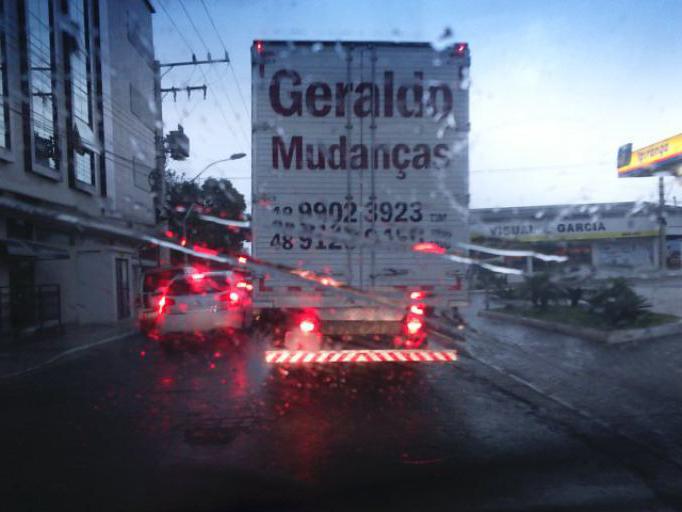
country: BR
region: Santa Catarina
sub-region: Itapema
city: Itapema
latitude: -27.1309
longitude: -48.6061
